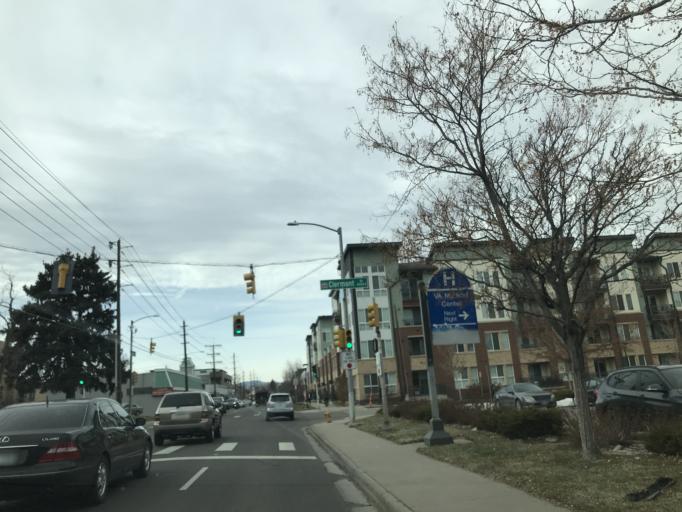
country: US
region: Colorado
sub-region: Arapahoe County
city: Glendale
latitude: 39.7293
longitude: -104.9346
